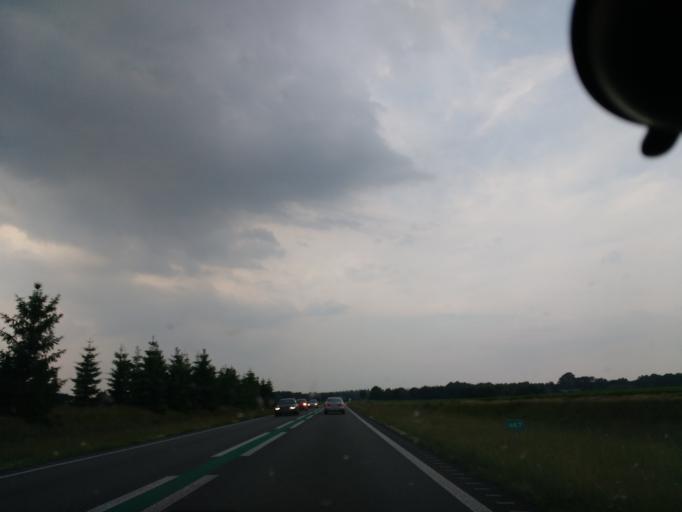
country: NL
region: Drenthe
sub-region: Gemeente Coevorden
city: Sleen
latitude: 52.8361
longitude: 6.8352
